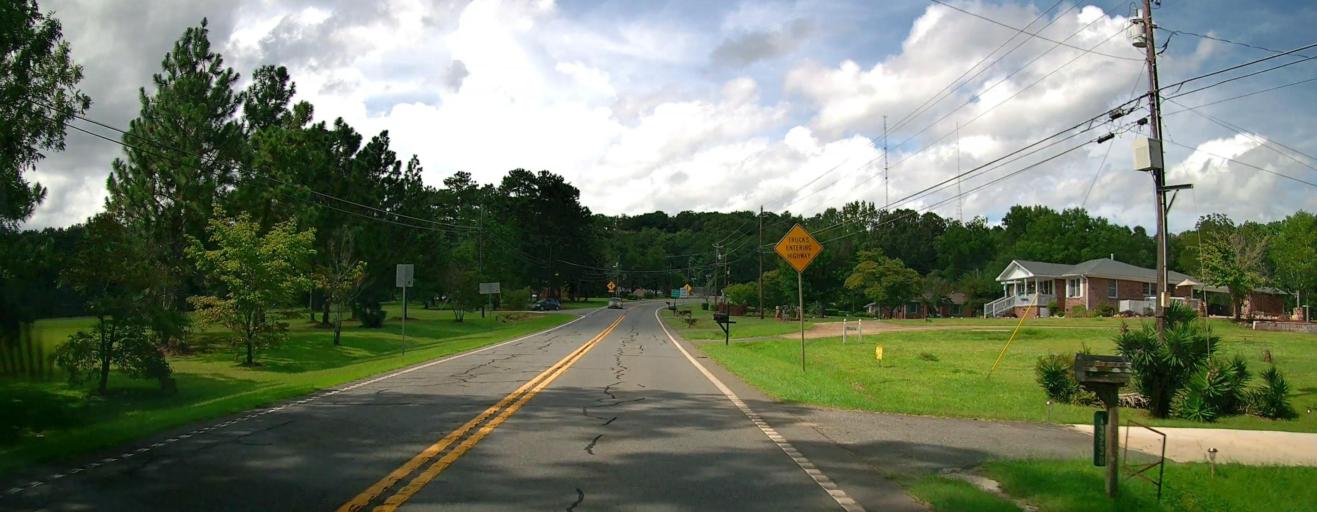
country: US
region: Georgia
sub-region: Meriwether County
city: Manchester
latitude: 32.8391
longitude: -84.6227
